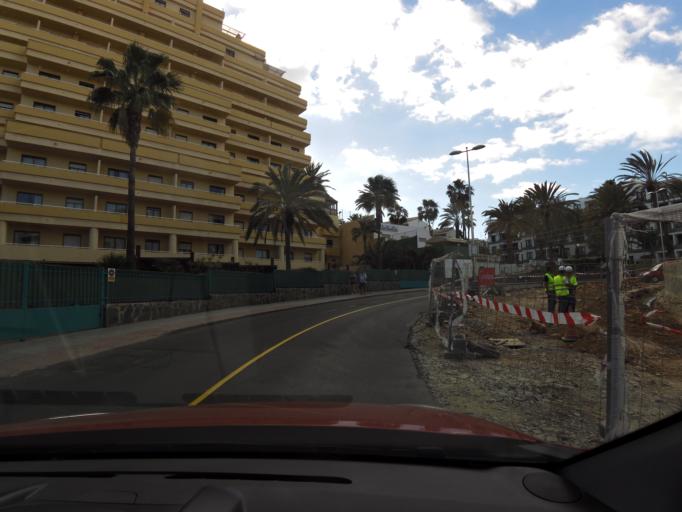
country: ES
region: Canary Islands
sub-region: Provincia de Las Palmas
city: Playa del Ingles
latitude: 27.7578
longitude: -15.5719
